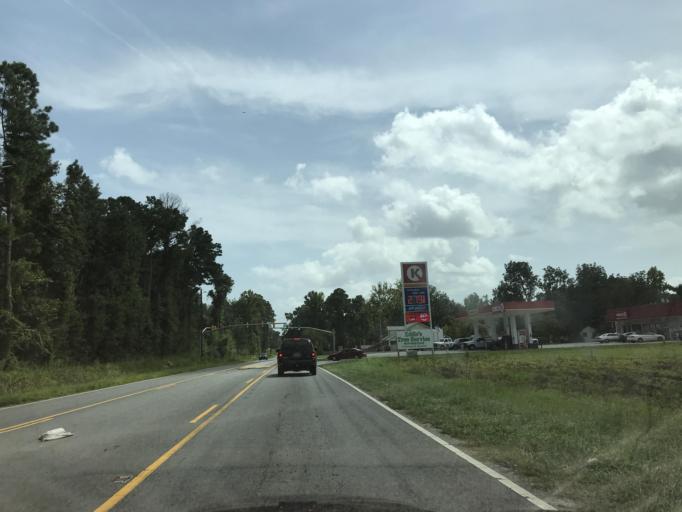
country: US
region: North Carolina
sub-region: New Hanover County
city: Wrightsboro
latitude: 34.3034
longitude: -77.9218
